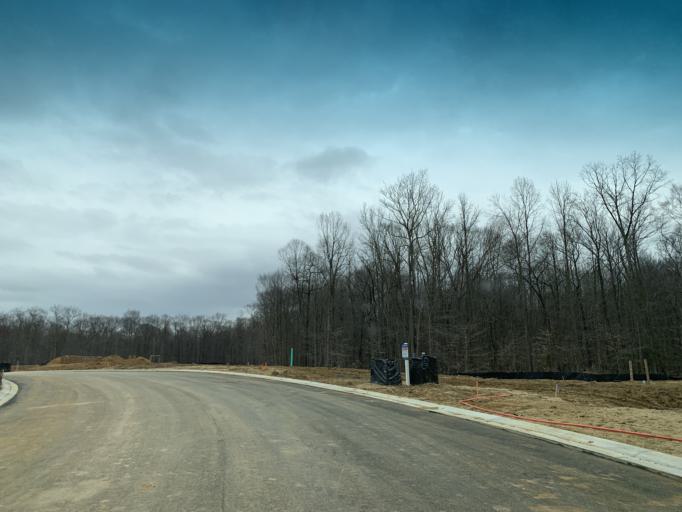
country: US
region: Maryland
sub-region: Harford County
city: Perryman
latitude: 39.4992
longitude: -76.2028
